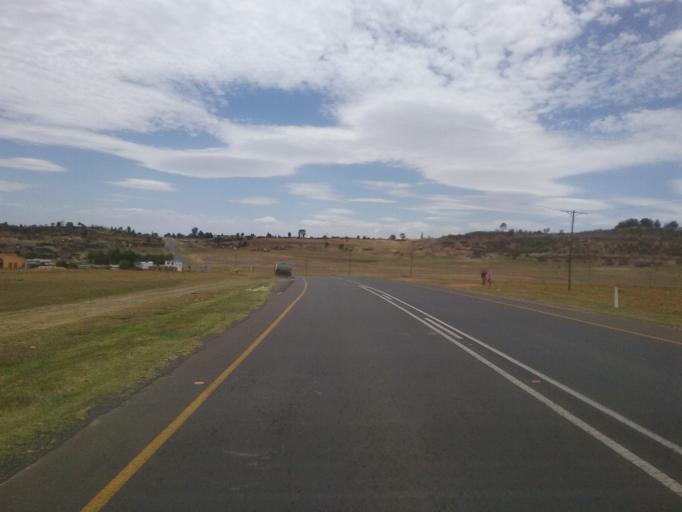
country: LS
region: Maseru
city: Maseru
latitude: -29.5034
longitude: 27.5287
